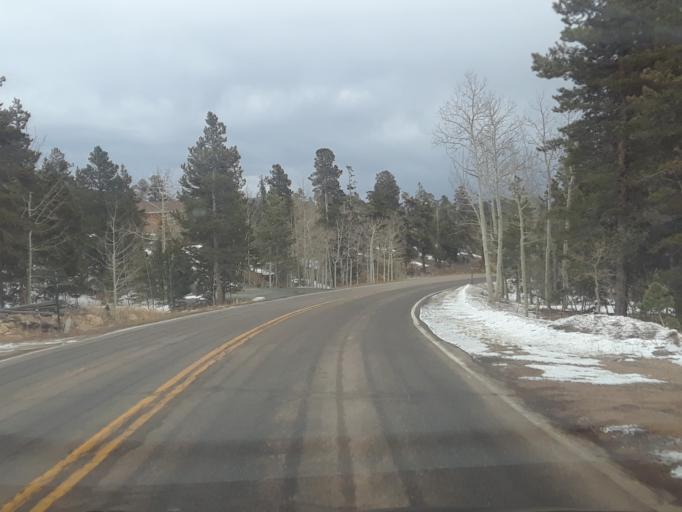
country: US
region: Colorado
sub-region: Gilpin County
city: Central City
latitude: 39.8406
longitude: -105.4707
